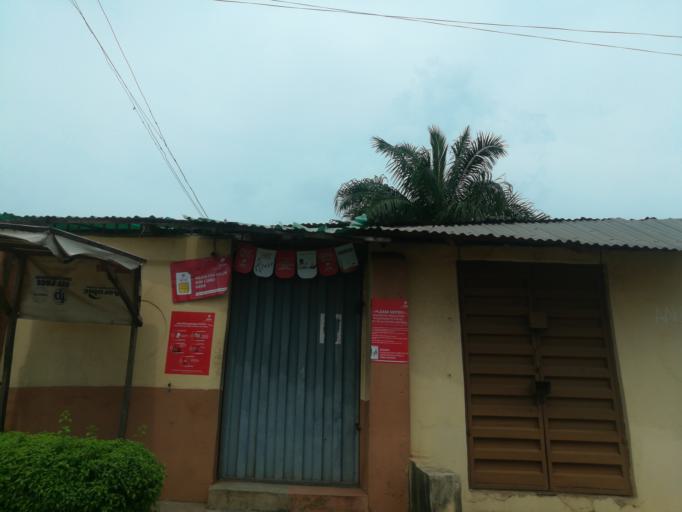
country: NG
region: Oyo
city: Ibadan
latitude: 7.4300
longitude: 3.9228
